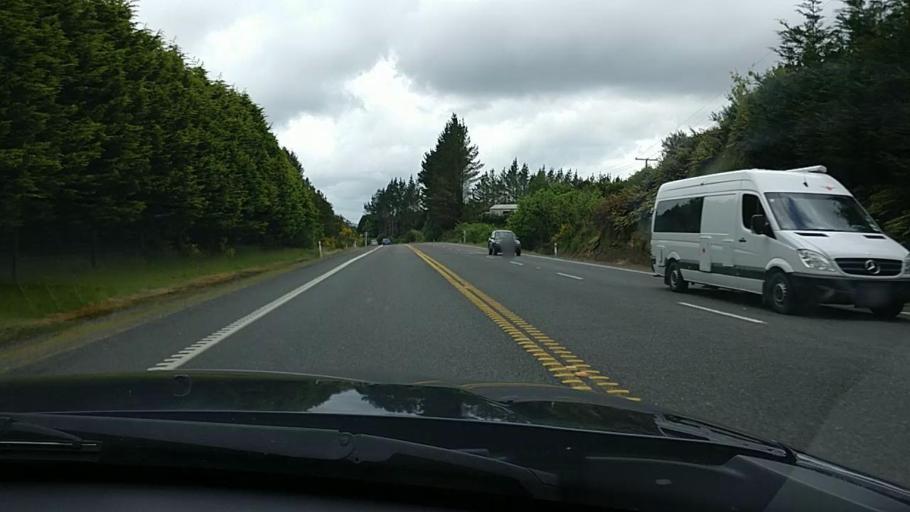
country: NZ
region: Bay of Plenty
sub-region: Rotorua District
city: Rotorua
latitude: -38.0636
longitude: 176.0987
